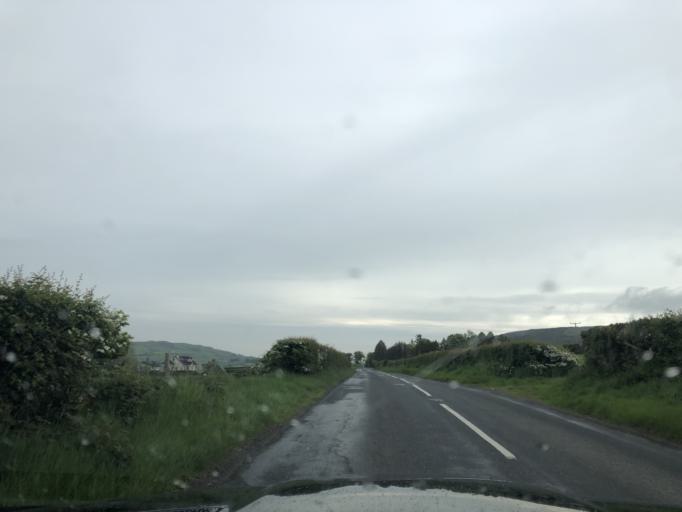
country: GB
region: Northern Ireland
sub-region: Down District
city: Castlewellan
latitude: 54.2177
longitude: -6.0277
